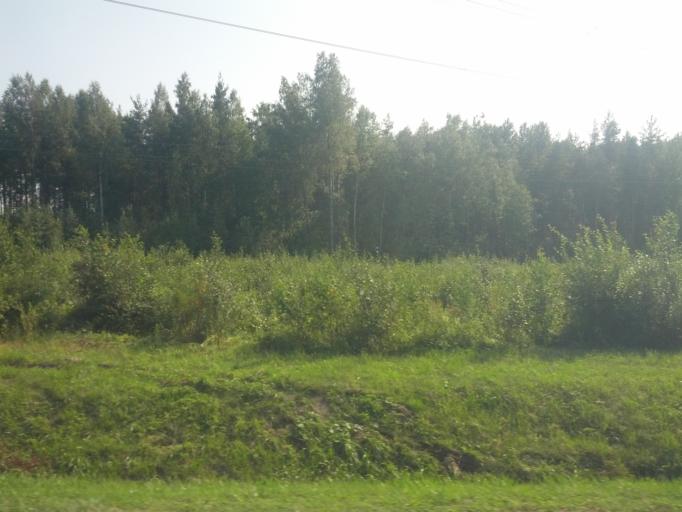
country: RU
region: Leningrad
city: Yanino Vtoroye
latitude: 59.8913
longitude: 30.5570
